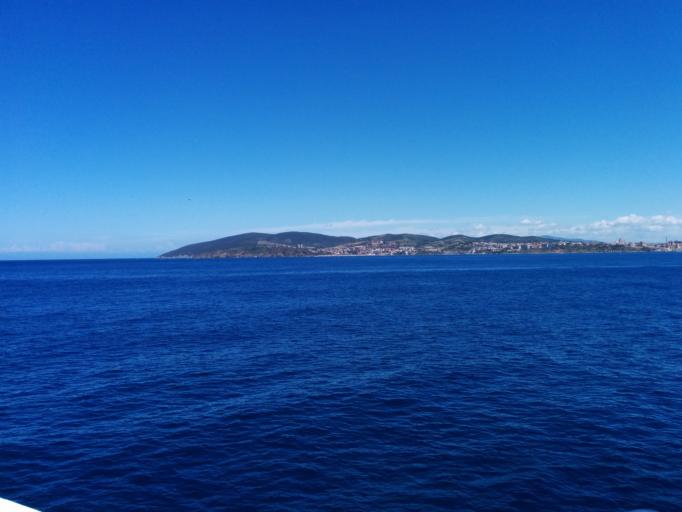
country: IT
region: Tuscany
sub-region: Provincia di Livorno
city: Piombino
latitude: 42.8985
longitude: 10.5022
